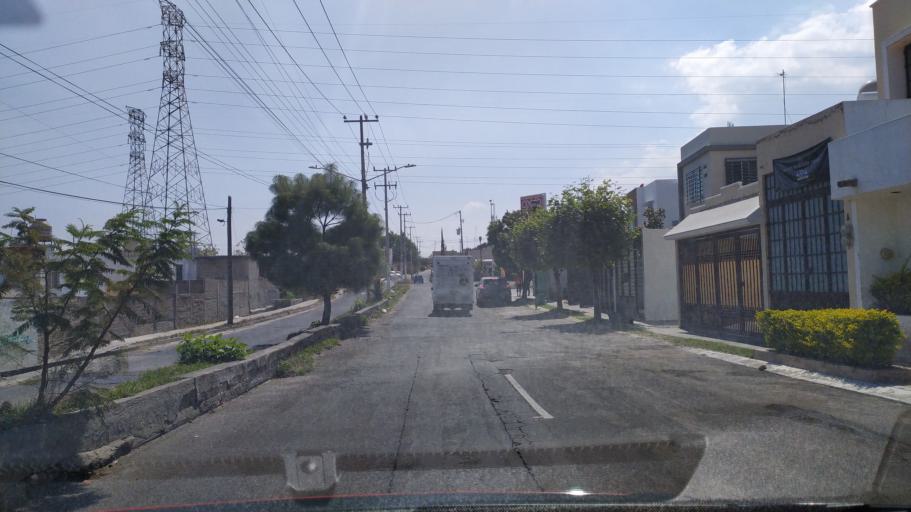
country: MX
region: Jalisco
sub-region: Zapopan
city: Campo Real
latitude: 20.7722
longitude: -103.4341
